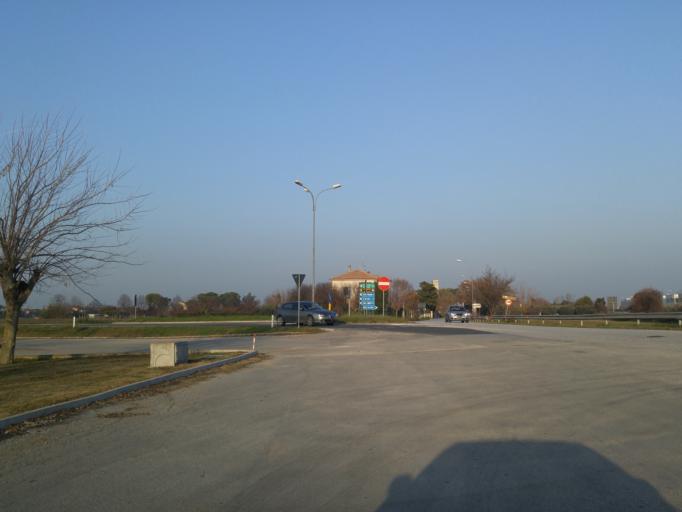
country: IT
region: The Marches
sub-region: Provincia di Pesaro e Urbino
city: Bellocchi
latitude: 43.7904
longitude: 12.9970
